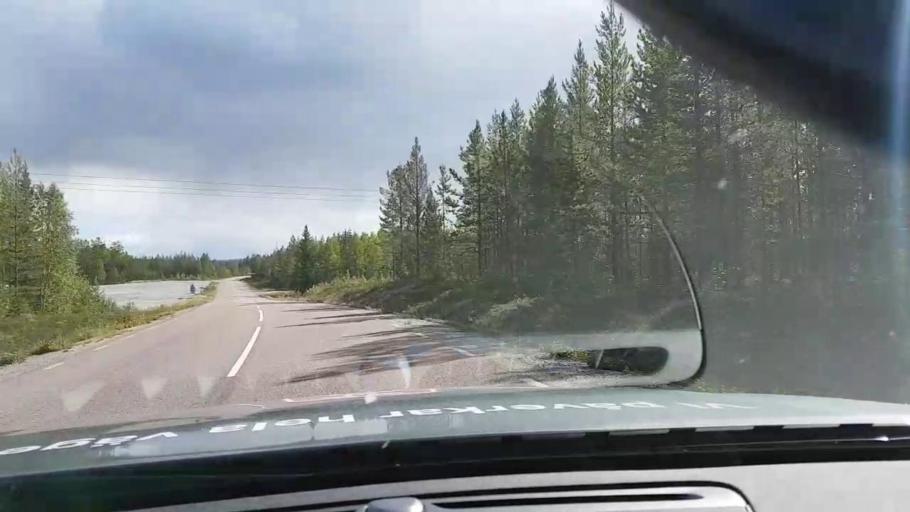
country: SE
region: Vaesterbotten
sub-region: Asele Kommun
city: Asele
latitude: 63.8891
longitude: 17.3487
